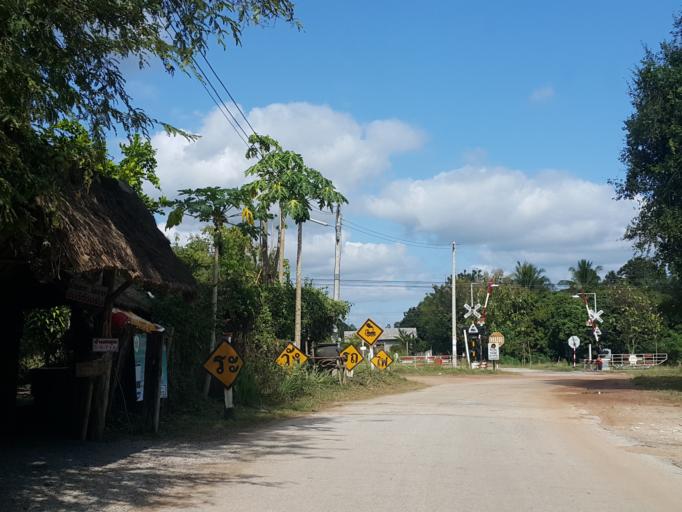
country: TH
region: Lampang
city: Hang Chat
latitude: 18.3412
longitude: 99.3591
